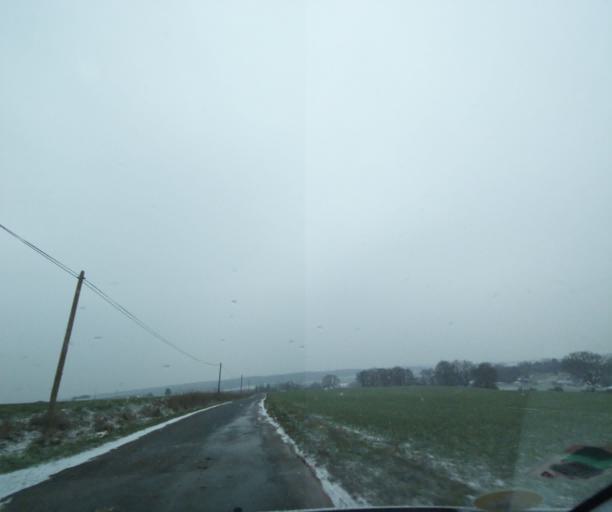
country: FR
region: Champagne-Ardenne
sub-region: Departement de la Haute-Marne
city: Wassy
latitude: 48.4702
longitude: 4.9816
